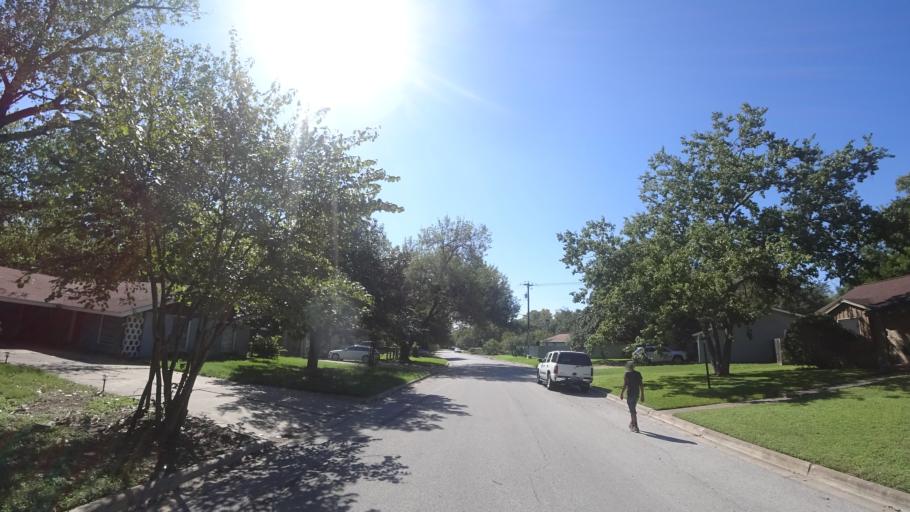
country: US
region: Texas
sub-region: Travis County
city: Austin
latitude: 30.3171
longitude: -97.6947
